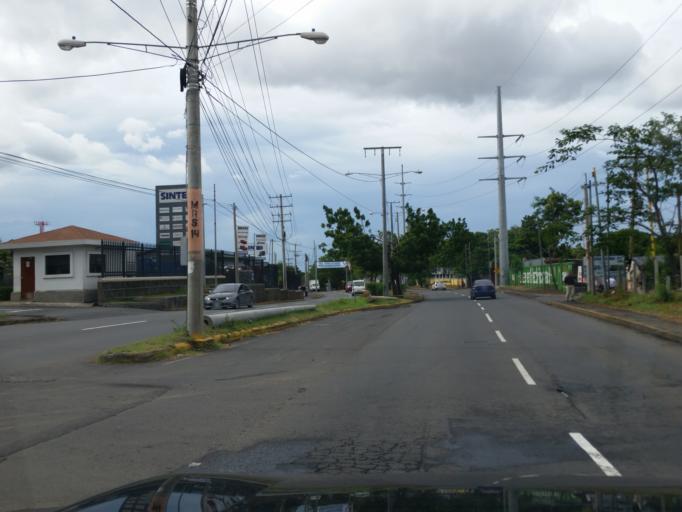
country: NI
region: Managua
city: Managua
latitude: 12.1229
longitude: -86.2837
